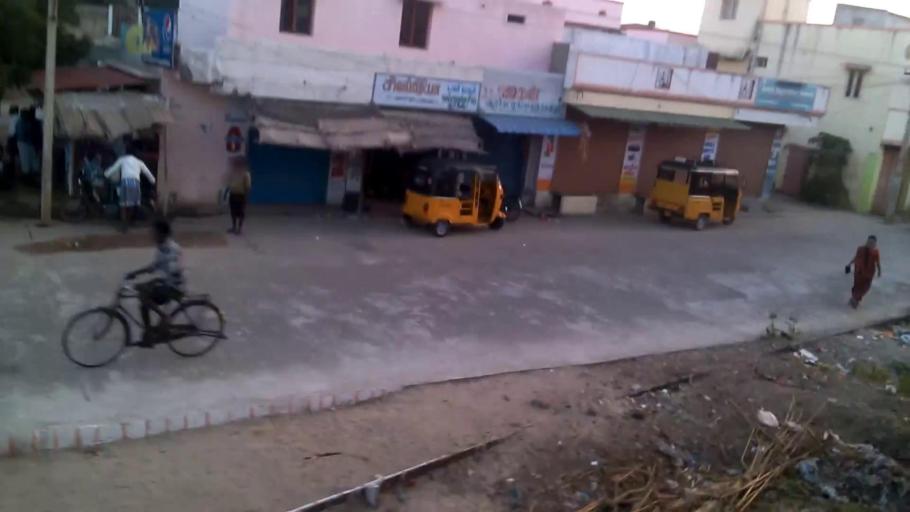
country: IN
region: Tamil Nadu
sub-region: Thoothukkudi
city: Korampallam
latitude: 8.8091
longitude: 78.1428
